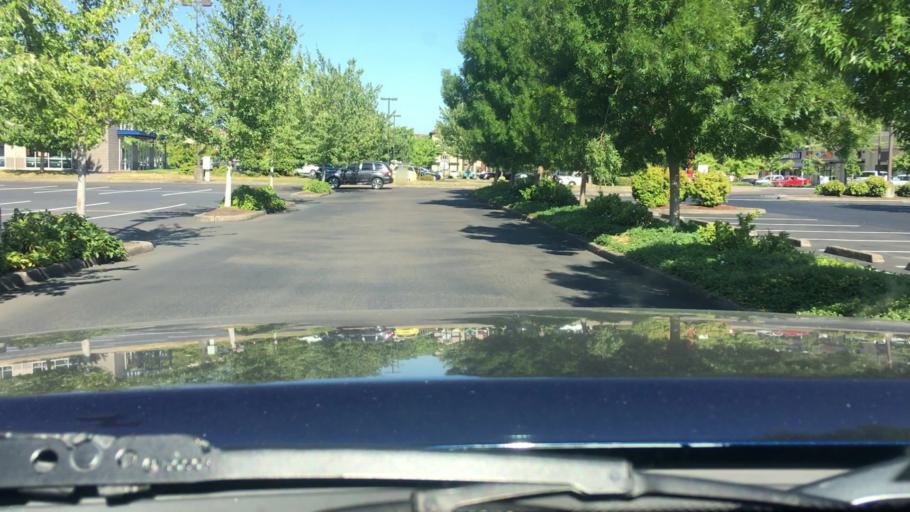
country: US
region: Oregon
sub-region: Lane County
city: Springfield
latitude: 44.0818
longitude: -123.0441
